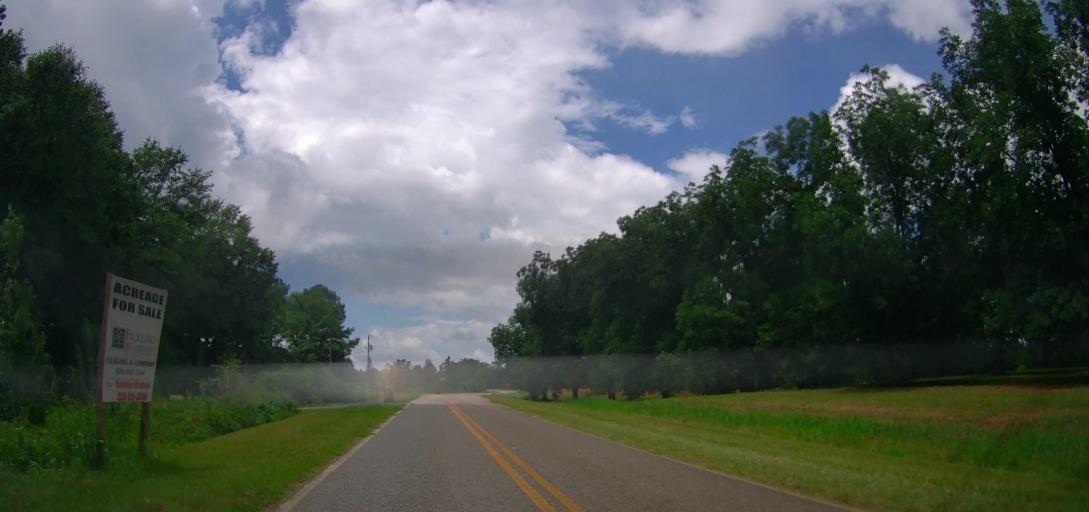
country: US
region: Georgia
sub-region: Pulaski County
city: Hawkinsville
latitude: 32.3473
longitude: -83.5711
